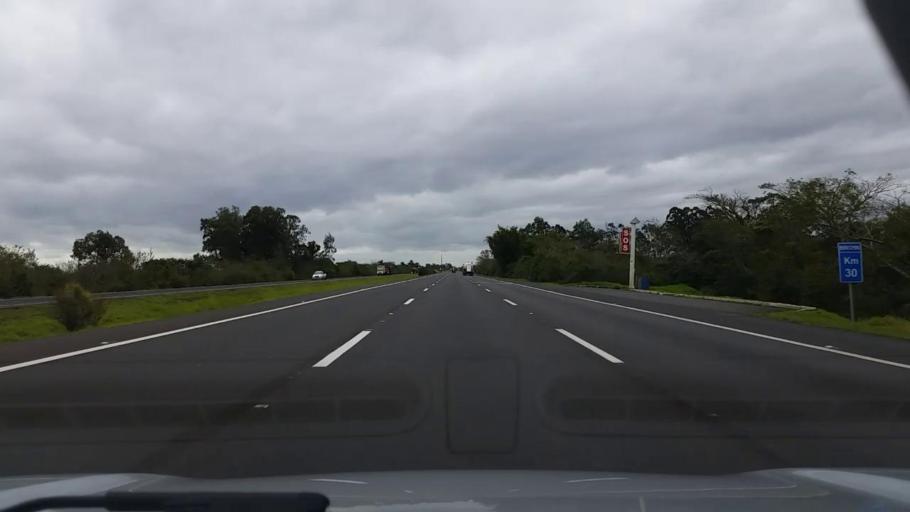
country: BR
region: Rio Grande do Sul
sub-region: Rolante
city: Rolante
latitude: -29.8836
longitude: -50.5549
